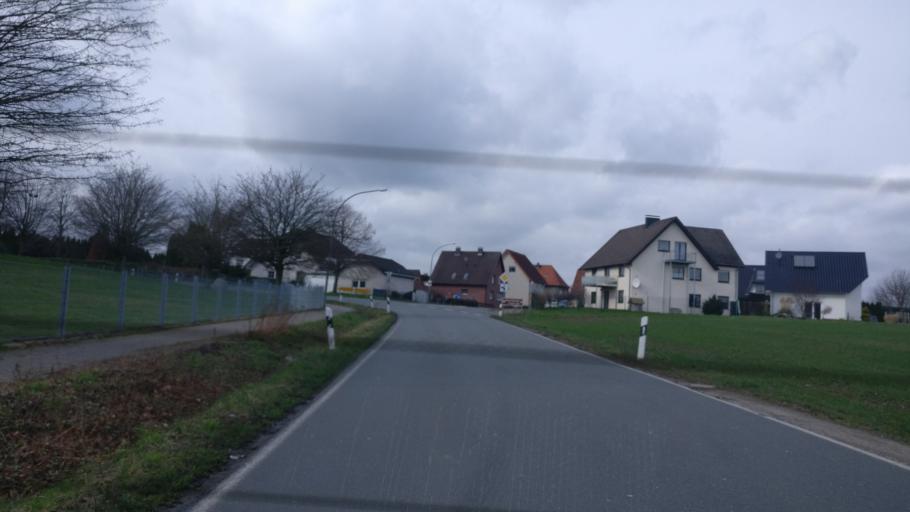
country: DE
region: North Rhine-Westphalia
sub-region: Regierungsbezirk Detmold
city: Lage
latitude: 52.0170
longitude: 8.7886
